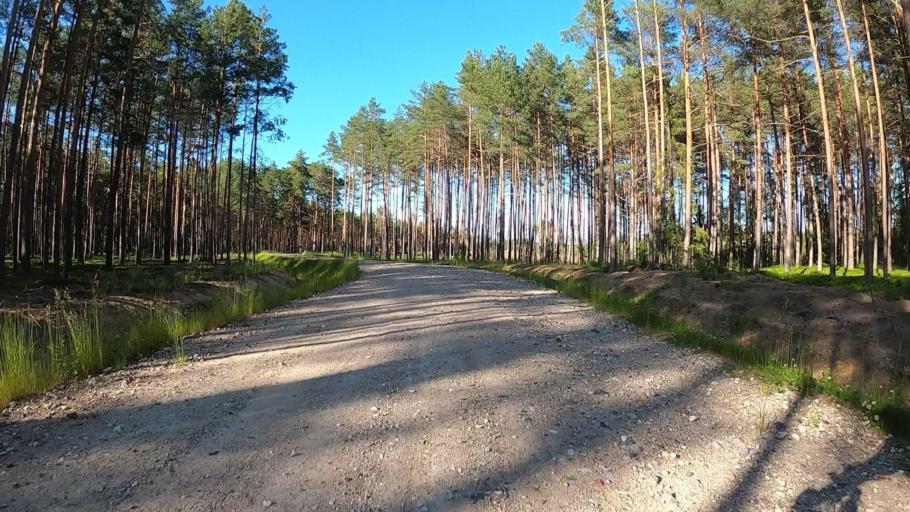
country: LV
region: Carnikava
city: Carnikava
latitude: 57.1051
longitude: 24.2460
